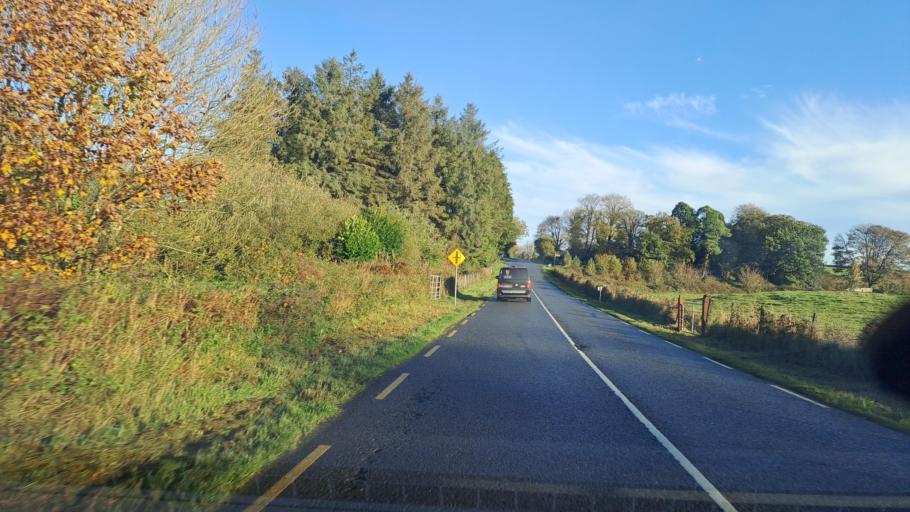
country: IE
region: Ulster
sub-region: County Monaghan
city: Monaghan
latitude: 54.1750
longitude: -6.9968
